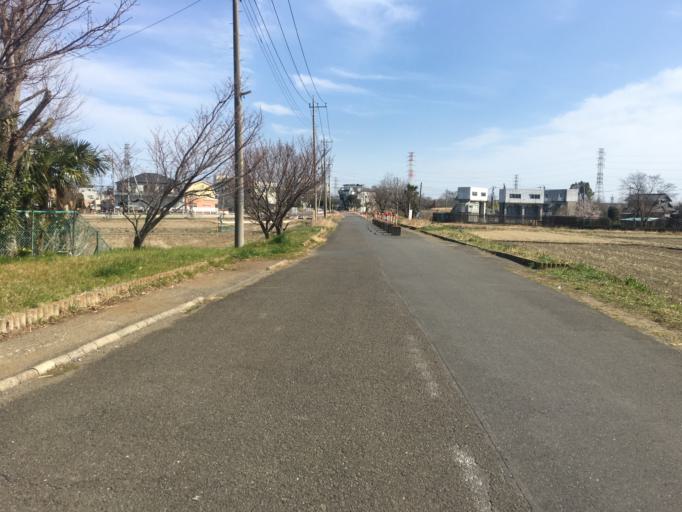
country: JP
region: Saitama
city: Shiki
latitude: 35.8309
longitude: 139.5933
